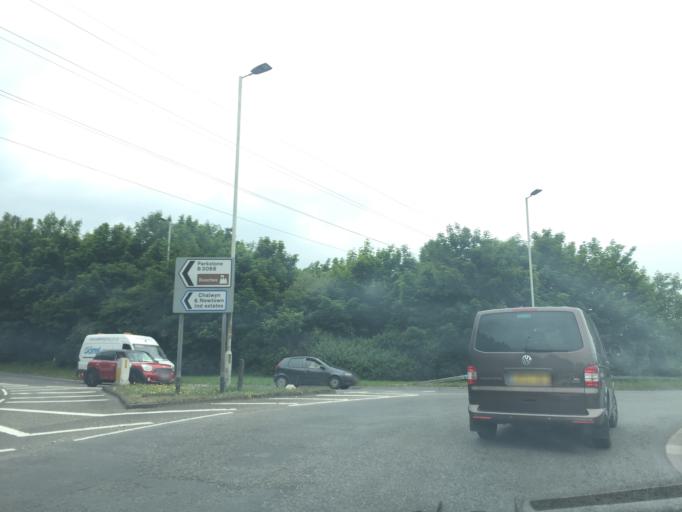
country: GB
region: England
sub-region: Dorset
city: Parkstone
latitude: 50.7508
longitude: -1.9360
